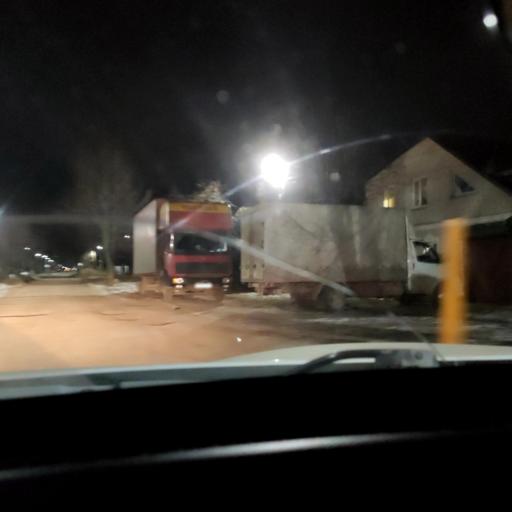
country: RU
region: Tatarstan
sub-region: Gorod Kazan'
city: Kazan
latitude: 55.8789
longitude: 49.0676
